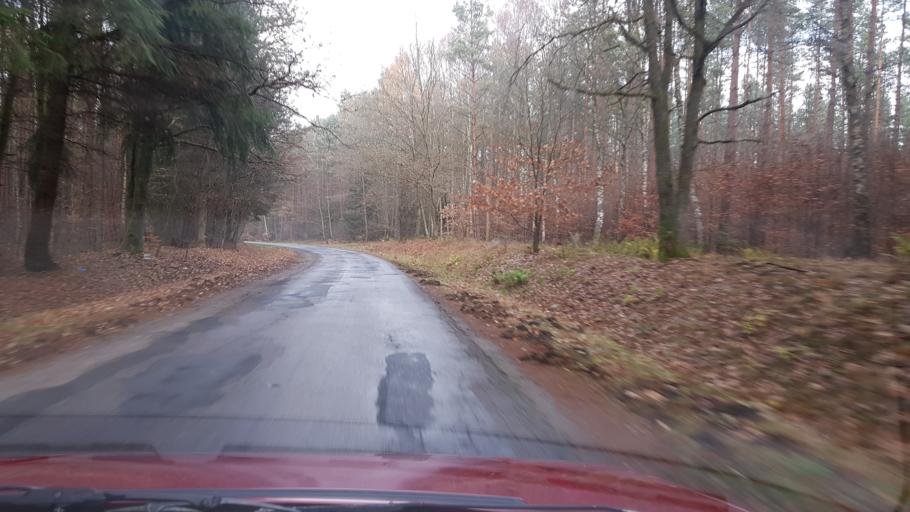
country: PL
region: West Pomeranian Voivodeship
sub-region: Powiat bialogardzki
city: Tychowo
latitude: 53.9691
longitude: 16.3147
